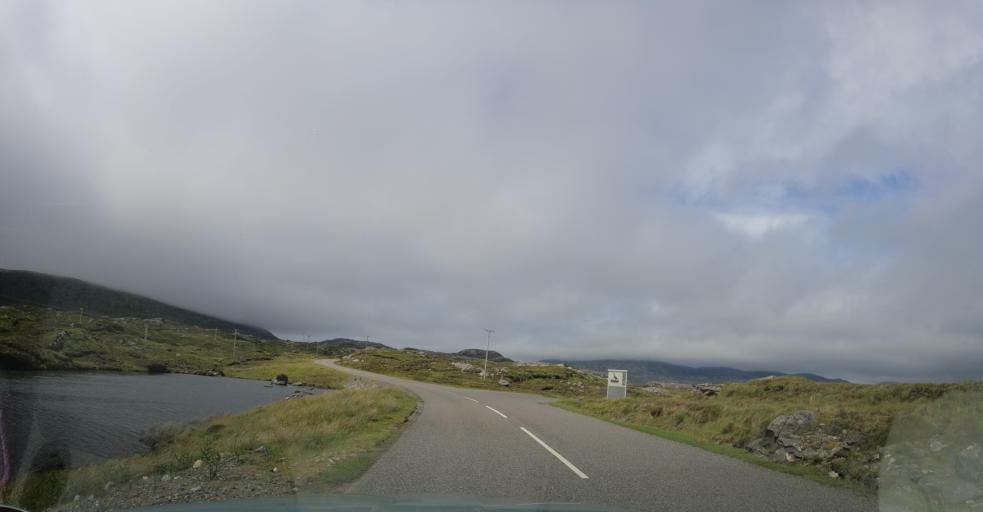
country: GB
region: Scotland
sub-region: Eilean Siar
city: Harris
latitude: 57.8718
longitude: -6.8171
